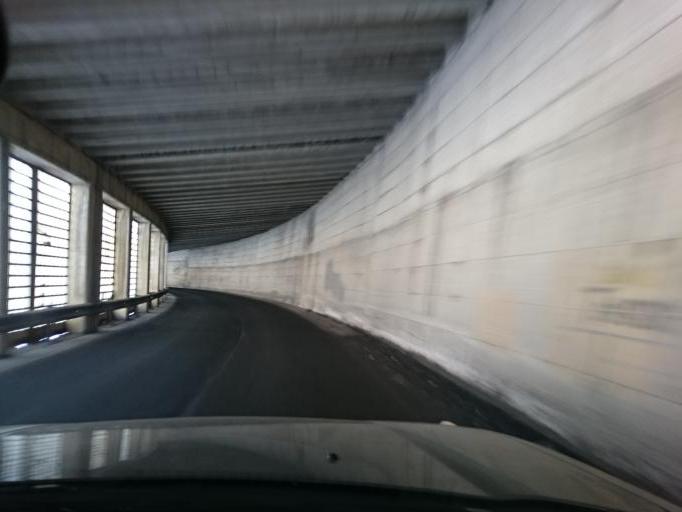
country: IT
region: Lombardy
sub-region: Provincia di Sondrio
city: Livigno
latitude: 46.5878
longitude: 10.1696
